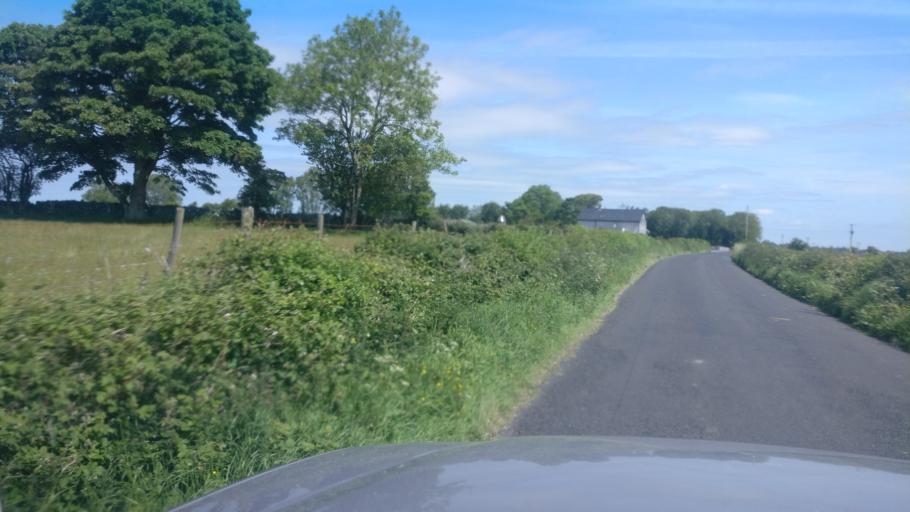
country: IE
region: Connaught
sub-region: County Galway
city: Gort
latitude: 53.1392
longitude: -8.7649
